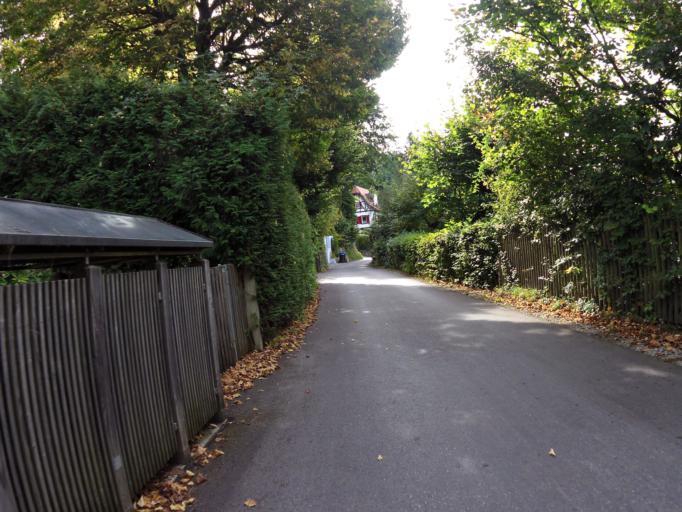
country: DE
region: Bavaria
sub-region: Upper Bavaria
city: Berg
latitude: 47.9493
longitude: 11.3418
